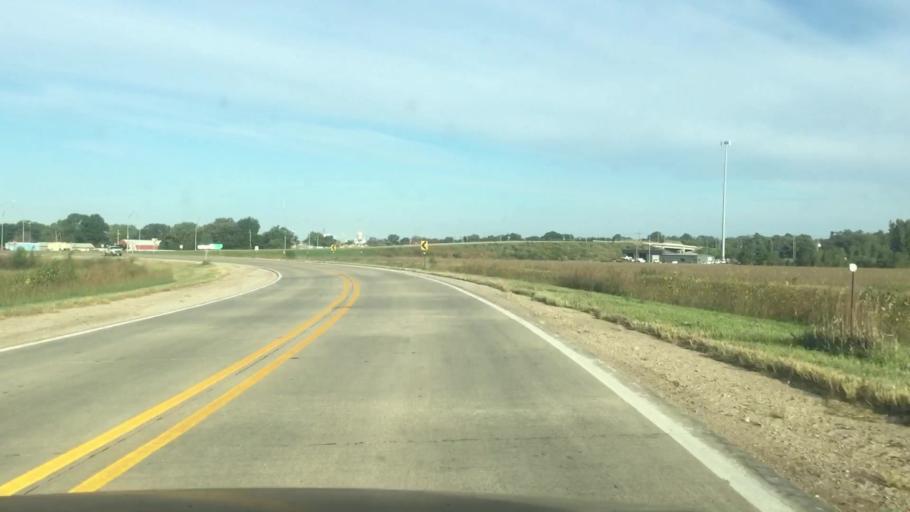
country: US
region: Nebraska
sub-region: Jefferson County
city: Fairbury
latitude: 40.1284
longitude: -97.1668
